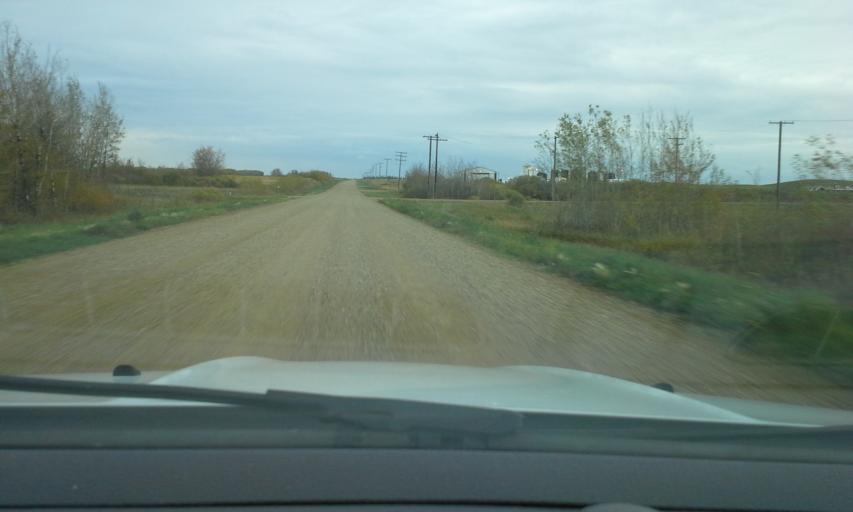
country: CA
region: Saskatchewan
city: Lloydminster
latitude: 53.2915
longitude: -109.8085
